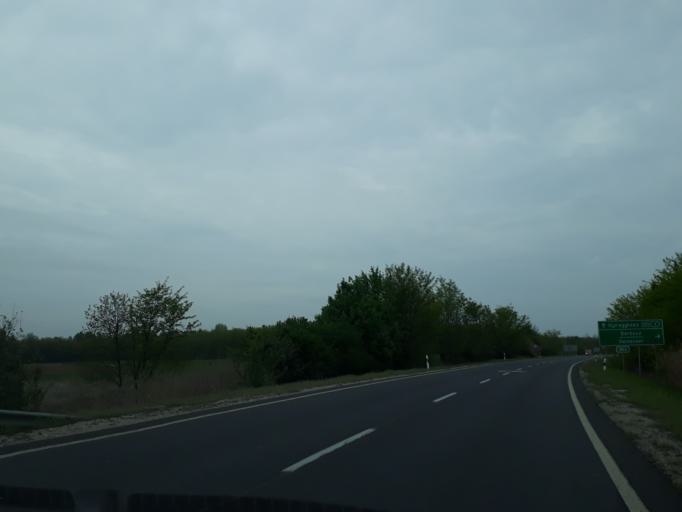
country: HU
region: Szabolcs-Szatmar-Bereg
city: Nyirtass
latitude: 48.0823
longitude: 21.9823
